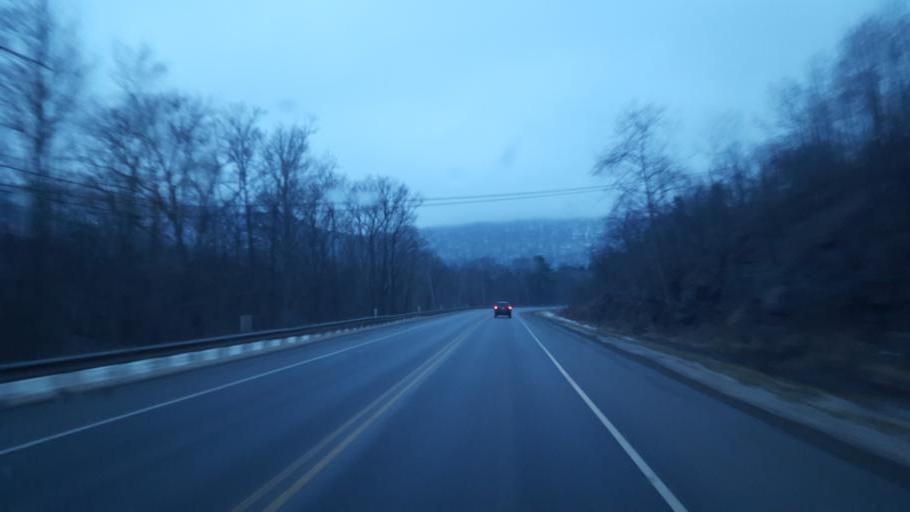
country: US
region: Pennsylvania
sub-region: McKean County
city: Port Allegany
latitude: 41.7903
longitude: -78.2332
